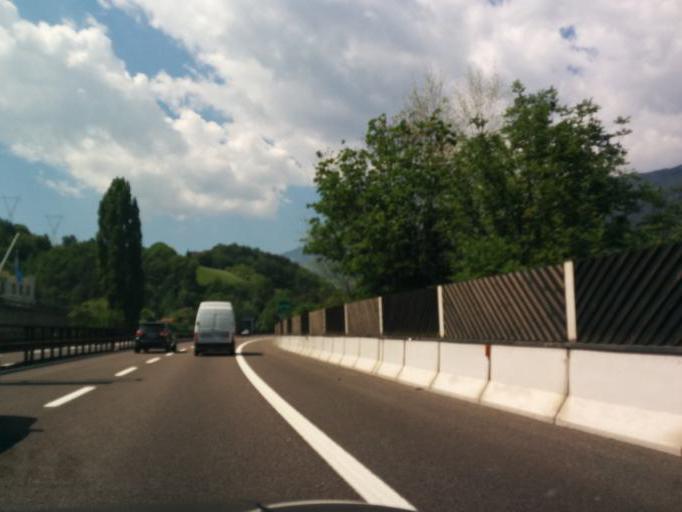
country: IT
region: Trentino-Alto Adige
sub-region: Bolzano
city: Chiusa
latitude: 46.6446
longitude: 11.5842
